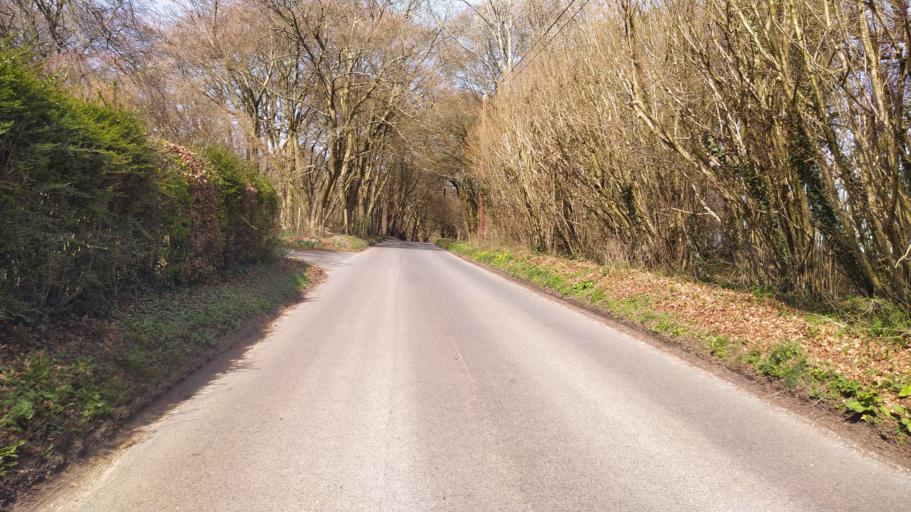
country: GB
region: England
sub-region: Hampshire
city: Four Marks
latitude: 51.0623
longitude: -1.1069
